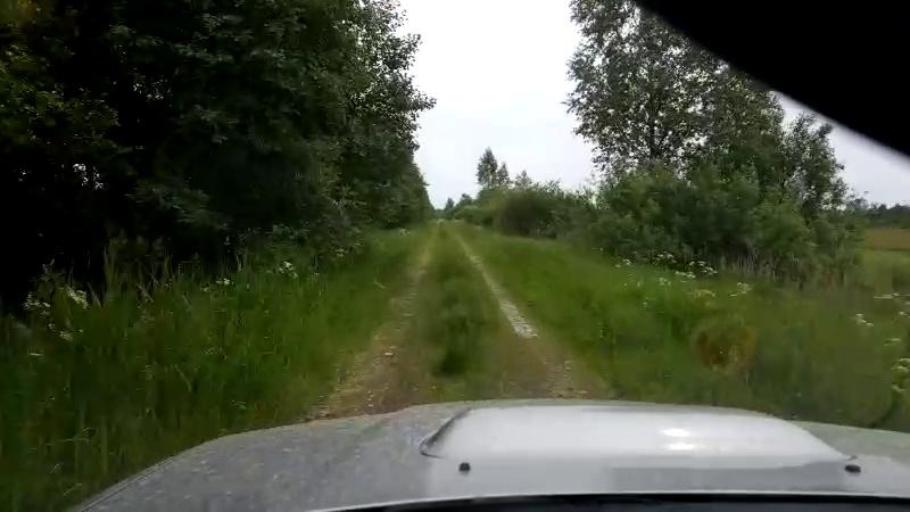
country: EE
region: Paernumaa
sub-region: Tootsi vald
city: Tootsi
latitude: 58.5651
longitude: 24.6890
